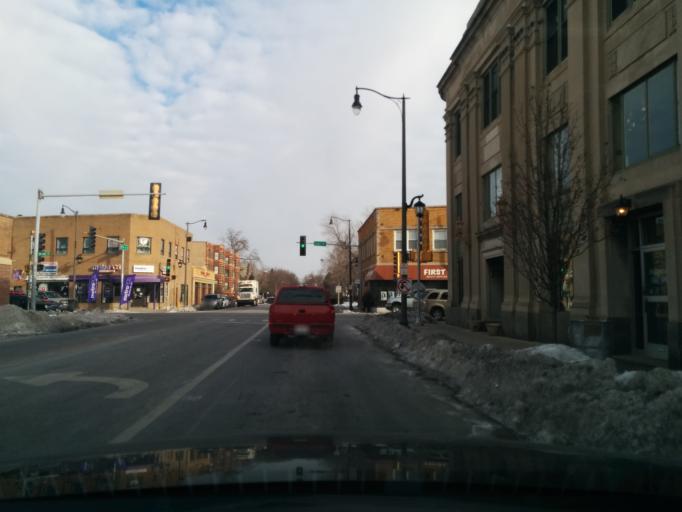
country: US
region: Illinois
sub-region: Cook County
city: Maywood
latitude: 41.8893
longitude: -87.8392
